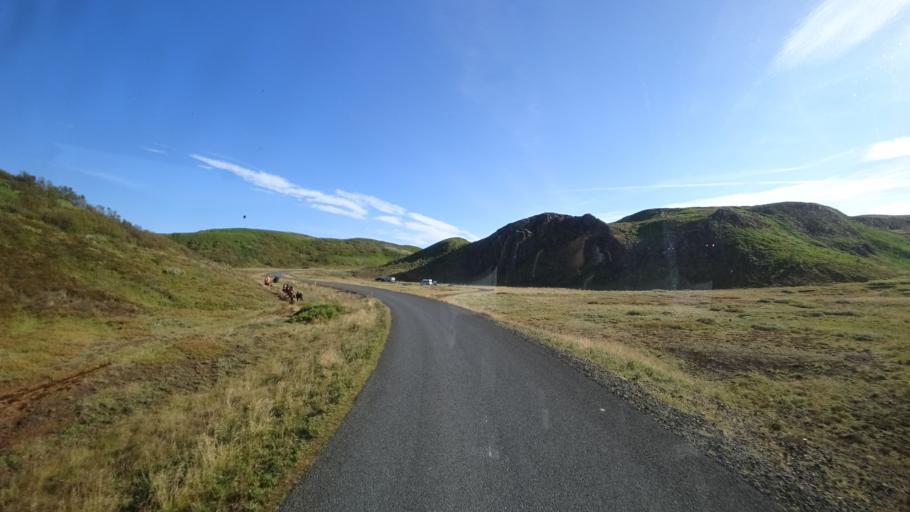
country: IS
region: South
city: Hveragerdi
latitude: 64.1386
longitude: -21.2557
